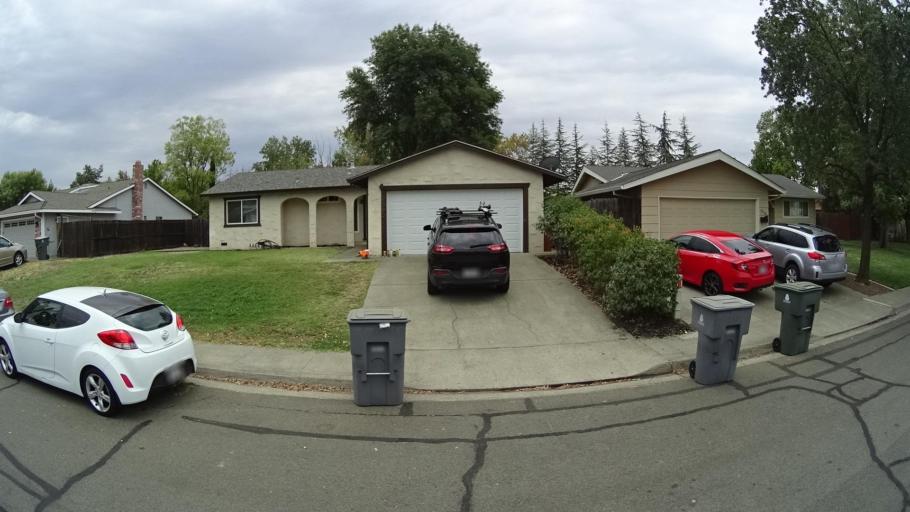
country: US
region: California
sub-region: Placer County
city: Rocklin
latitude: 38.7816
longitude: -121.2567
